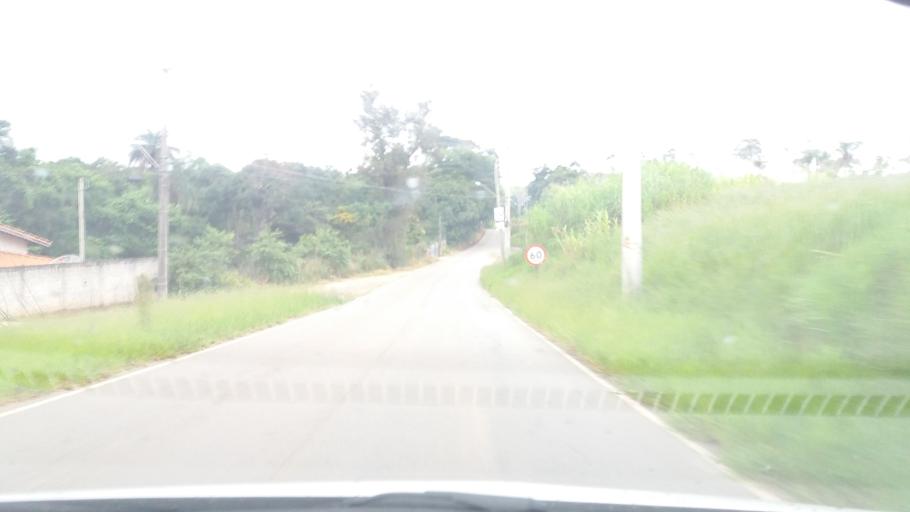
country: BR
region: Sao Paulo
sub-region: Bom Jesus Dos Perdoes
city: Bom Jesus dos Perdoes
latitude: -23.1710
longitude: -46.4389
